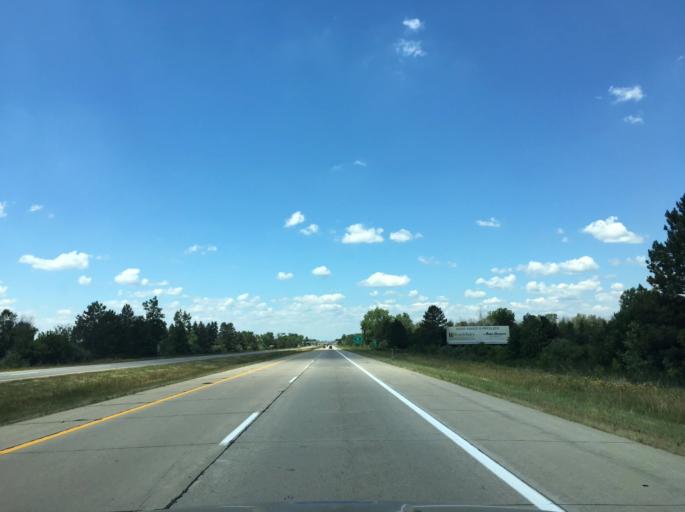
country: US
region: Michigan
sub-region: Bay County
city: Auburn
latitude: 43.5975
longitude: -84.1171
